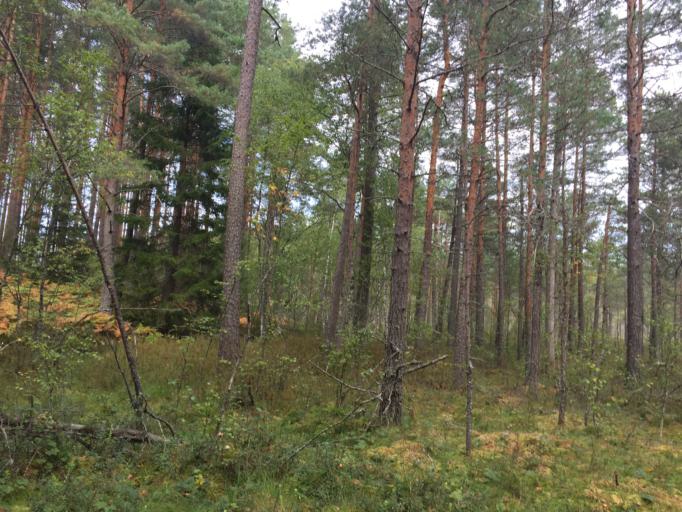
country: LV
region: Pargaujas
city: Stalbe
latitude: 57.3183
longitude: 25.0537
